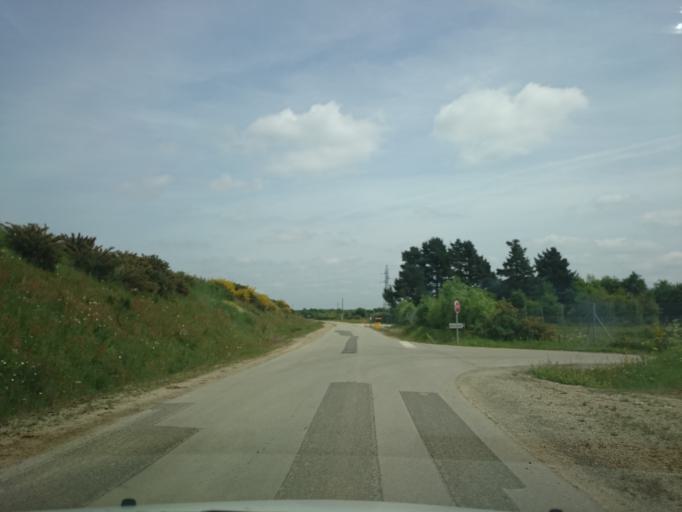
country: FR
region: Pays de la Loire
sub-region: Departement de la Loire-Atlantique
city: La Montagne
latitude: 47.1750
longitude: -1.6959
